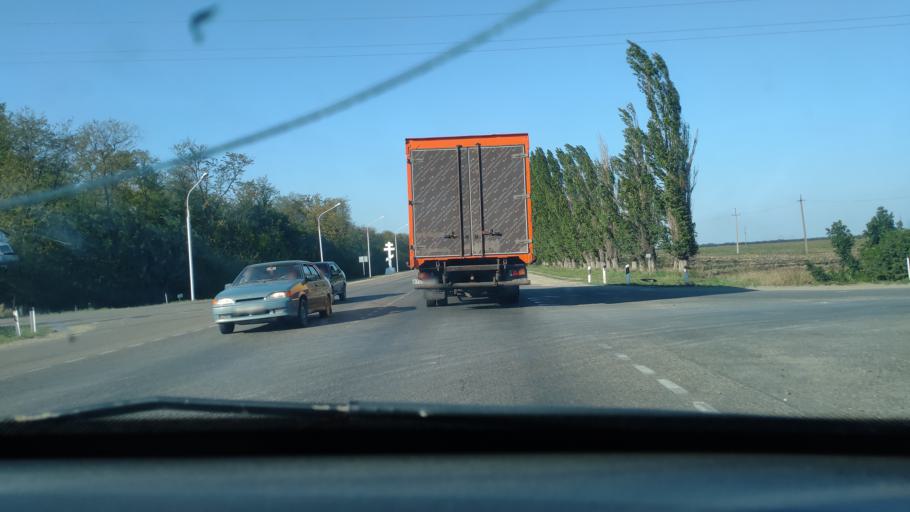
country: RU
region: Krasnodarskiy
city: Novotitarovskaya
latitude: 45.2607
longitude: 38.9993
